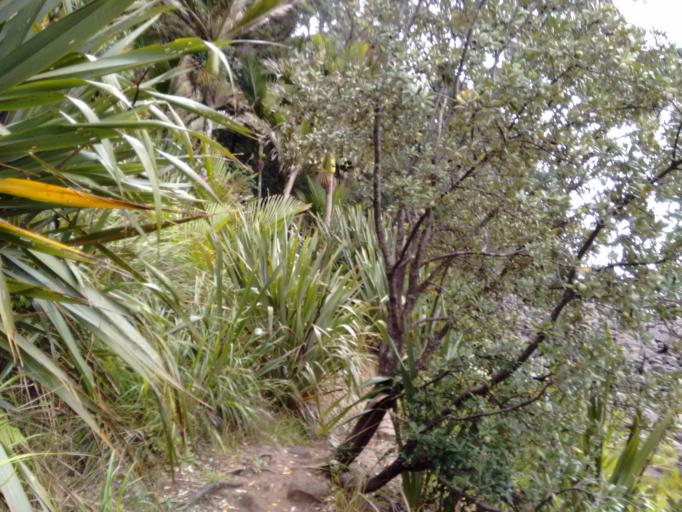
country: NZ
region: Waikato
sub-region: Thames-Coromandel District
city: Coromandel
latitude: -36.7029
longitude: 175.6110
